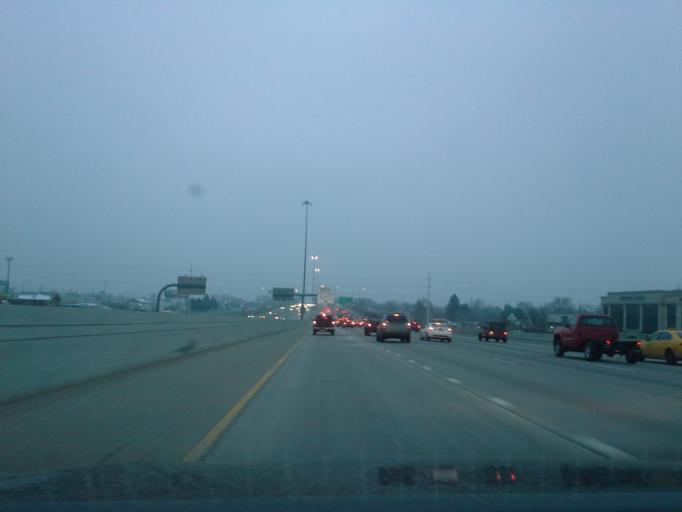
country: US
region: Utah
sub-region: Salt Lake County
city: Murray
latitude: 40.6501
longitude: -111.9023
